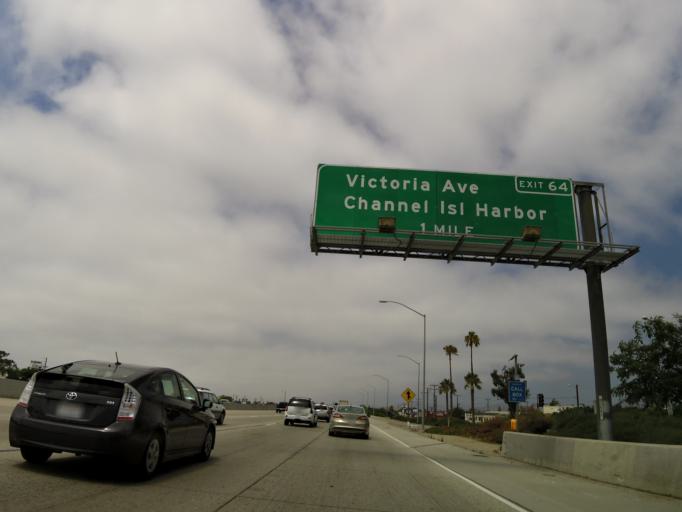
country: US
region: California
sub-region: Ventura County
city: El Rio
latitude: 34.2451
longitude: -119.1962
